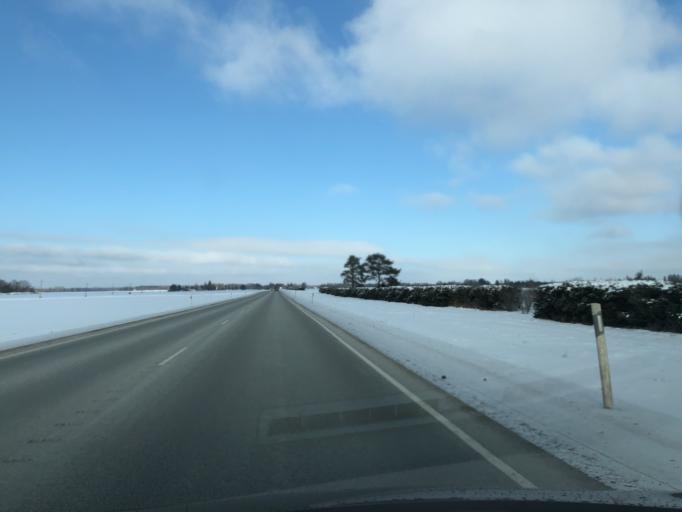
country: EE
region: Jaervamaa
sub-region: Paide linn
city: Paide
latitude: 58.7746
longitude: 25.7621
